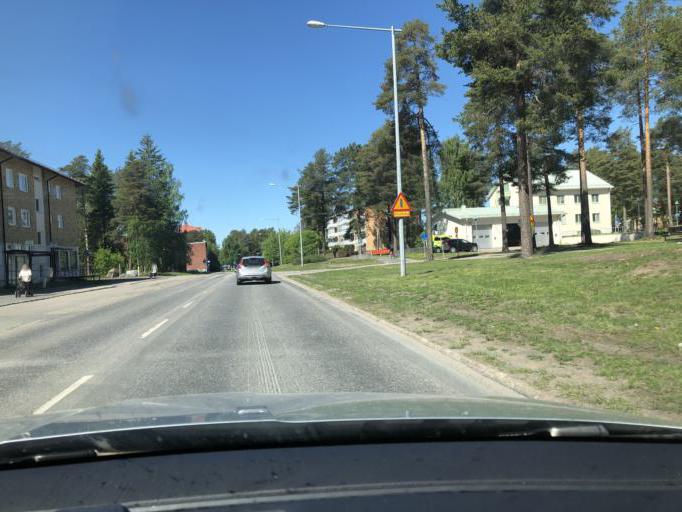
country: SE
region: Norrbotten
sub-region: Kalix Kommun
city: Kalix
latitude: 65.8533
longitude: 23.1553
